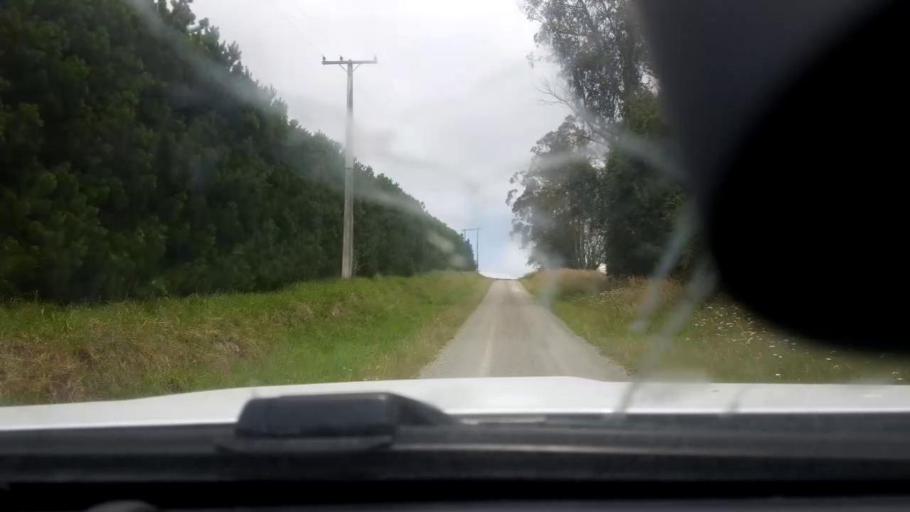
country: NZ
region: Canterbury
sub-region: Timaru District
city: Pleasant Point
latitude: -44.1685
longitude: 171.1458
